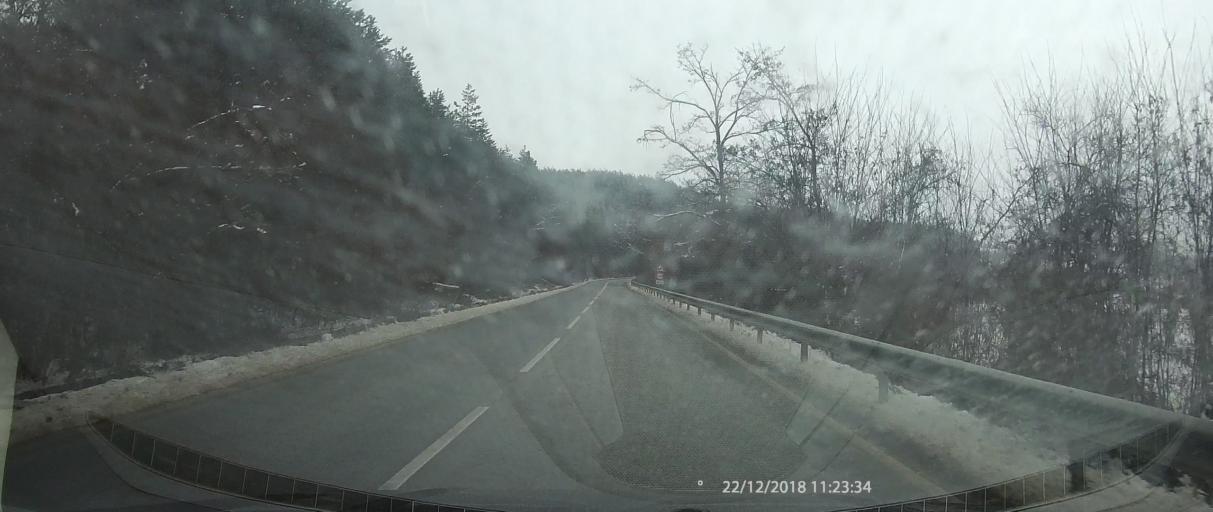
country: BG
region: Kyustendil
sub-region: Obshtina Boboshevo
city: Boboshevo
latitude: 42.2567
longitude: 22.8807
